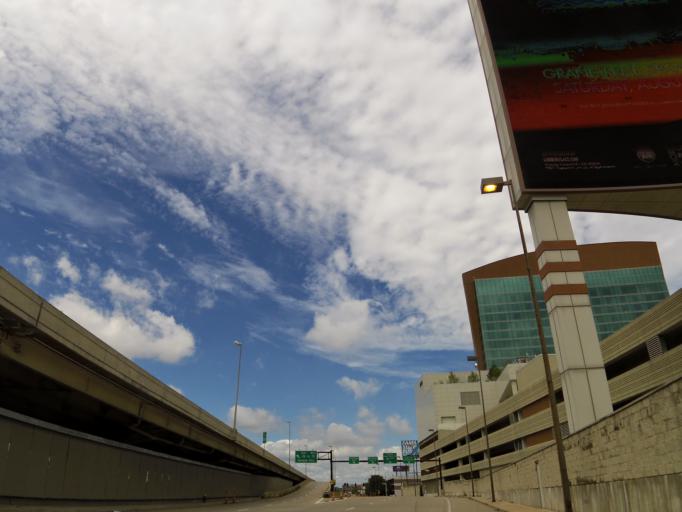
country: US
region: Missouri
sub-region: City of Saint Louis
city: St. Louis
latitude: 38.6323
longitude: -90.1859
